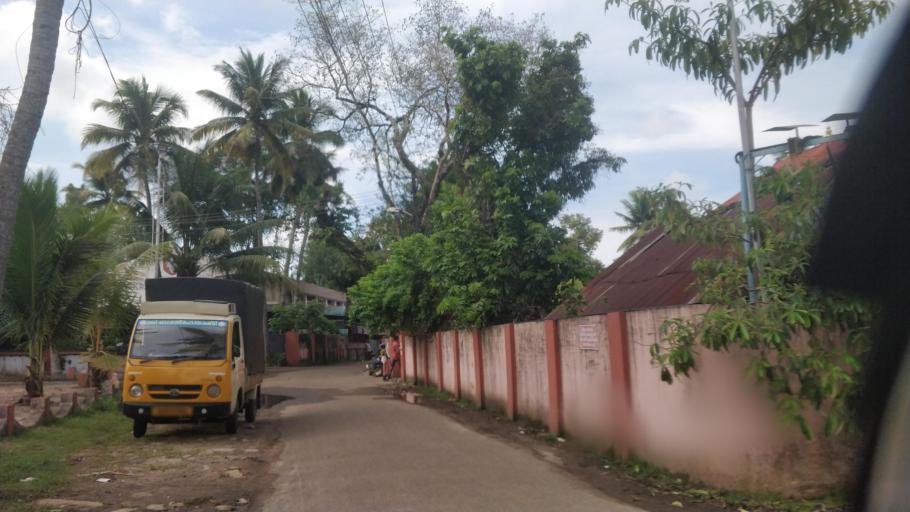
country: IN
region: Kerala
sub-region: Alappuzha
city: Vayalar
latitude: 9.6896
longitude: 76.3396
